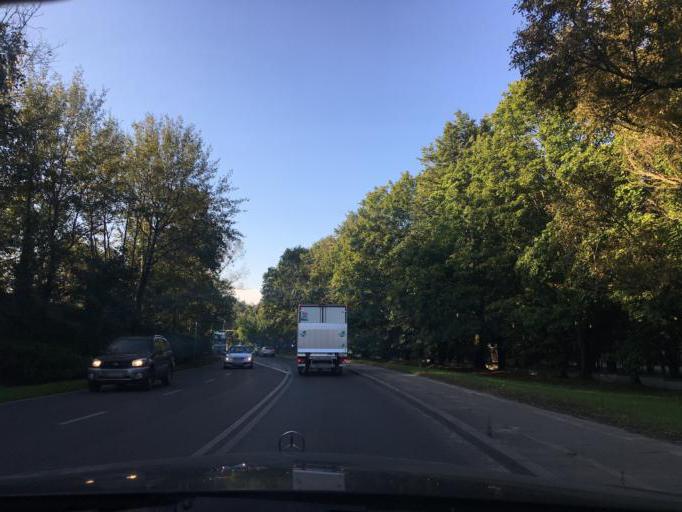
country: PL
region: Masovian Voivodeship
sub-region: Powiat pruszkowski
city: Granica
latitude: 52.1518
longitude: 20.7901
